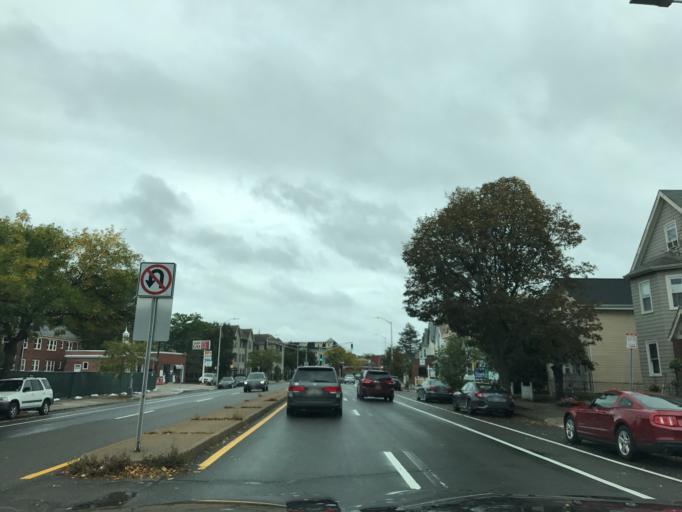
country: US
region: Massachusetts
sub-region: Middlesex County
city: Arlington
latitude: 42.4003
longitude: -71.1345
